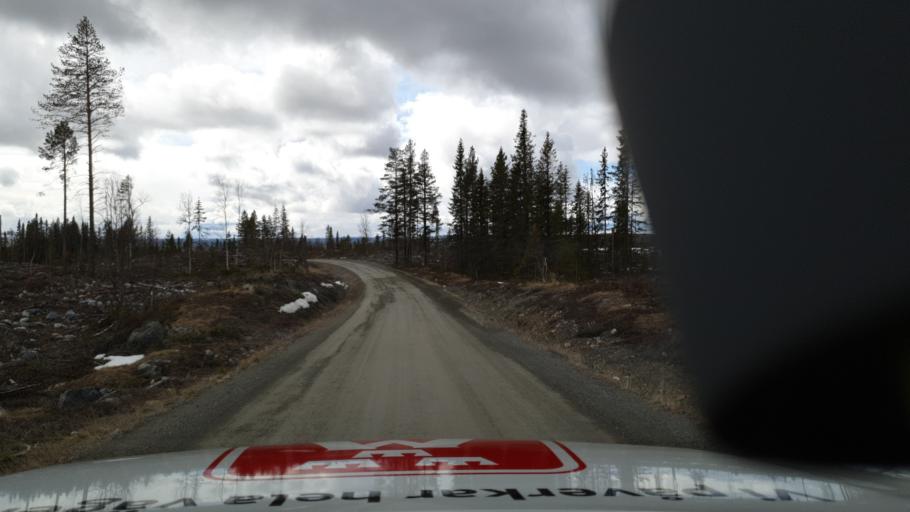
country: SE
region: Jaemtland
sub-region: Are Kommun
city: Jarpen
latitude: 62.8126
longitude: 13.8091
